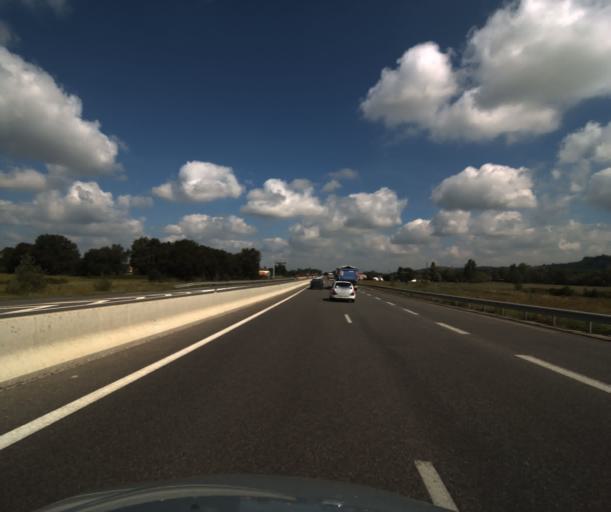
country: FR
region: Midi-Pyrenees
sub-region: Departement de la Haute-Garonne
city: Vernet
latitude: 43.4493
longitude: 1.4196
